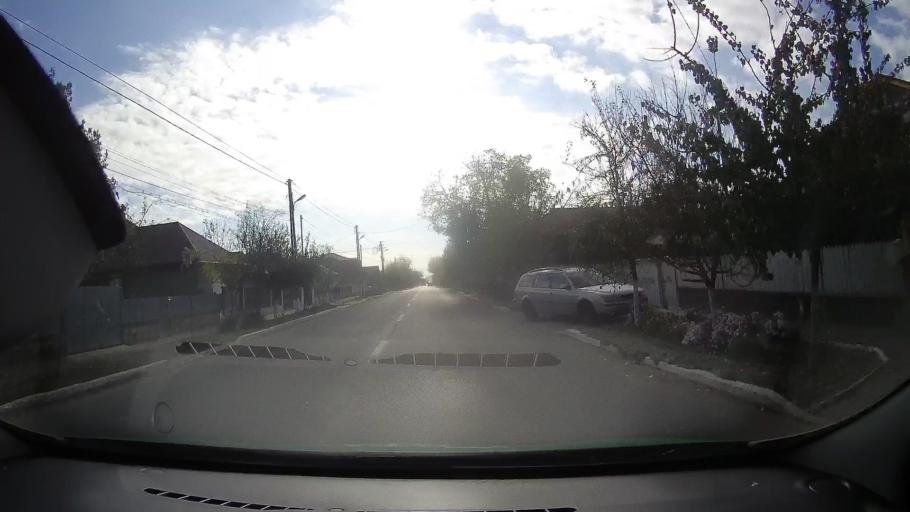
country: RO
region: Tulcea
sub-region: Comuna Sarichioi
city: Sarichioi
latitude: 44.9481
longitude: 28.8522
